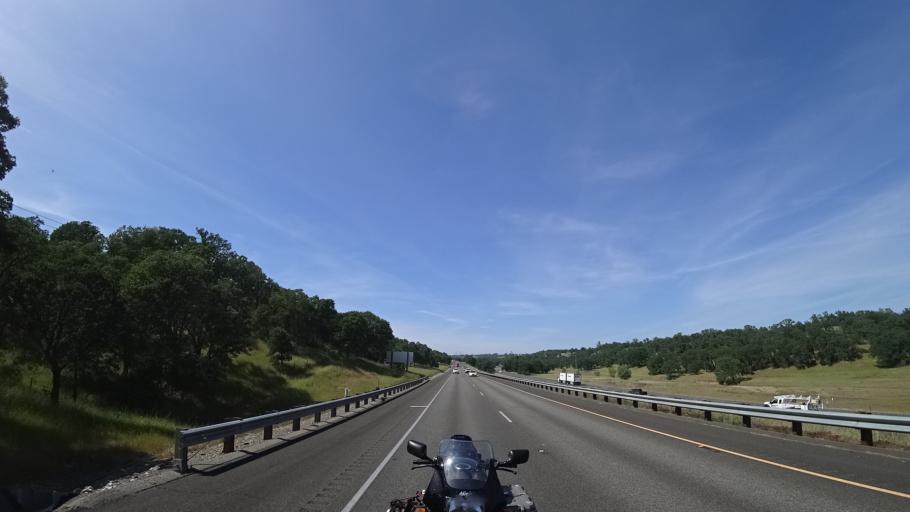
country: US
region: California
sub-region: Tehama County
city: Red Bluff
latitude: 40.2534
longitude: -122.2627
